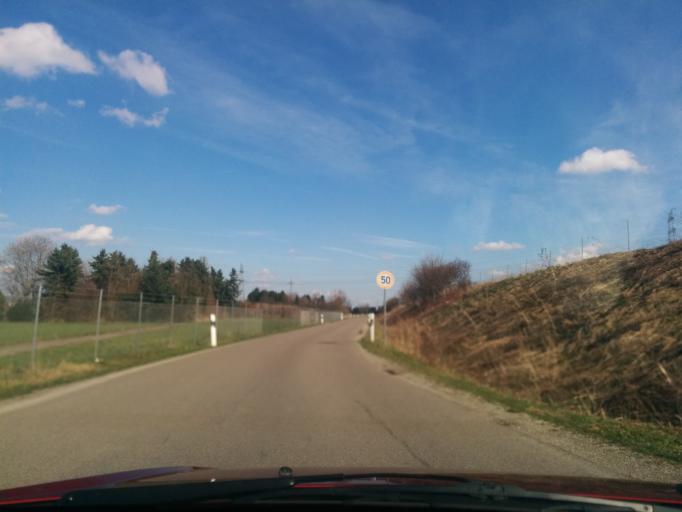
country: DE
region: Bavaria
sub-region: Upper Bavaria
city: Karlsfeld
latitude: 48.2046
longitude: 11.4324
